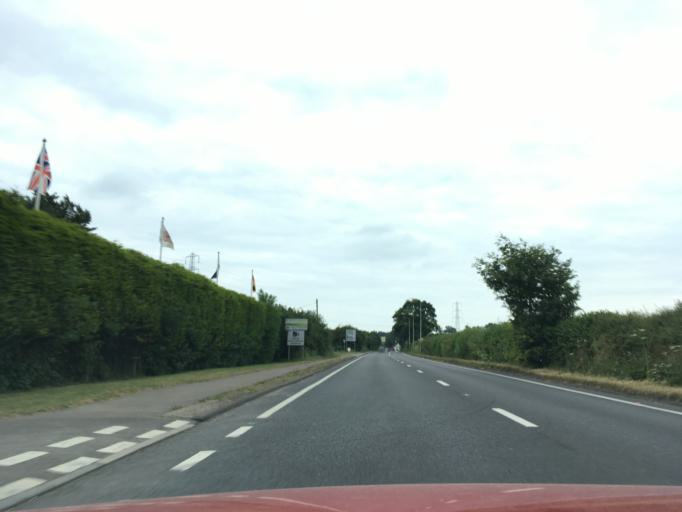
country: GB
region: England
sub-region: Hertfordshire
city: Markyate
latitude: 51.8539
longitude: -0.4786
